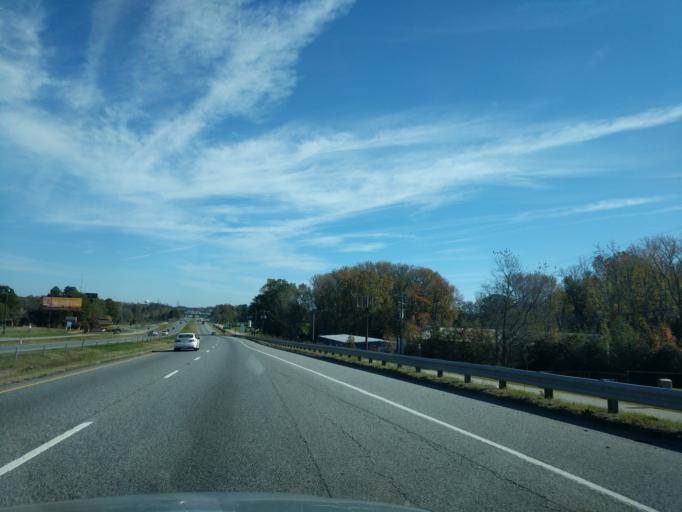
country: US
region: South Carolina
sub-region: Spartanburg County
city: Fairforest
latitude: 34.9648
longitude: -82.0181
